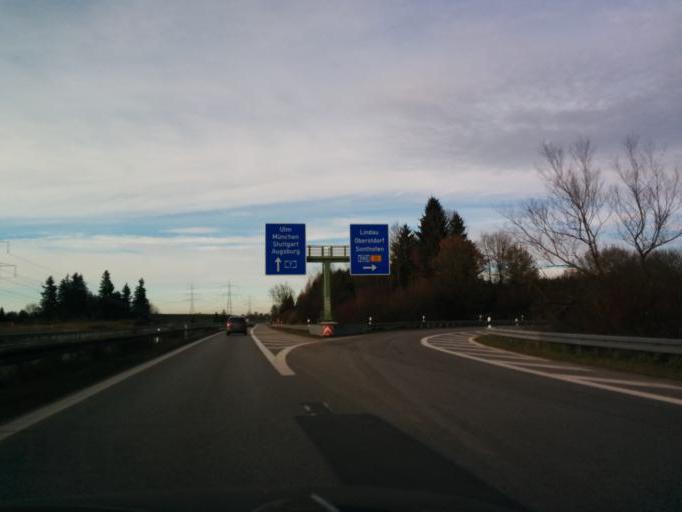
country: DE
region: Bavaria
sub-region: Swabia
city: Durach
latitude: 47.6878
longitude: 10.3680
